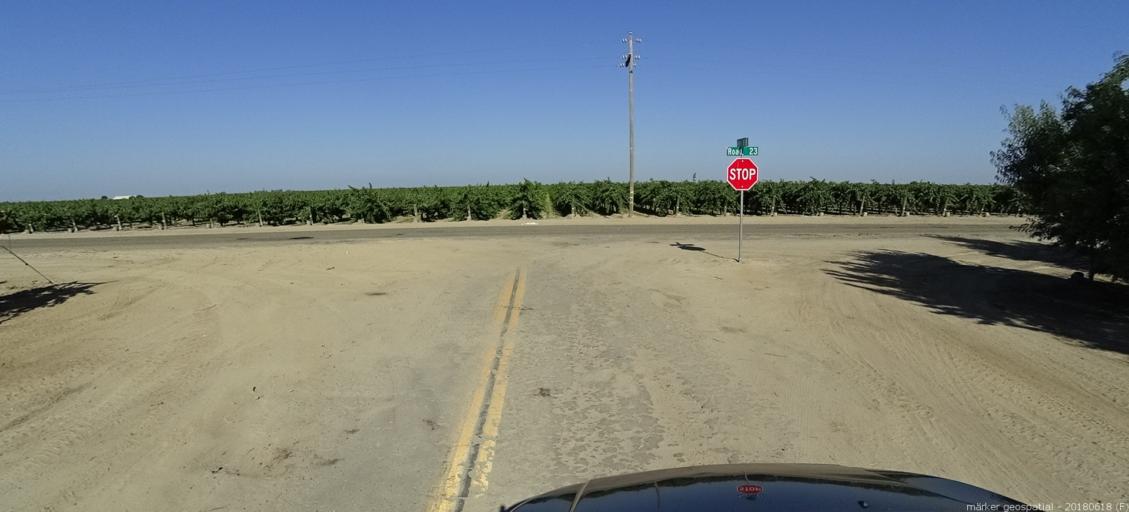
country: US
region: California
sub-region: Madera County
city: Parkwood
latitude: 36.8440
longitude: -120.1280
